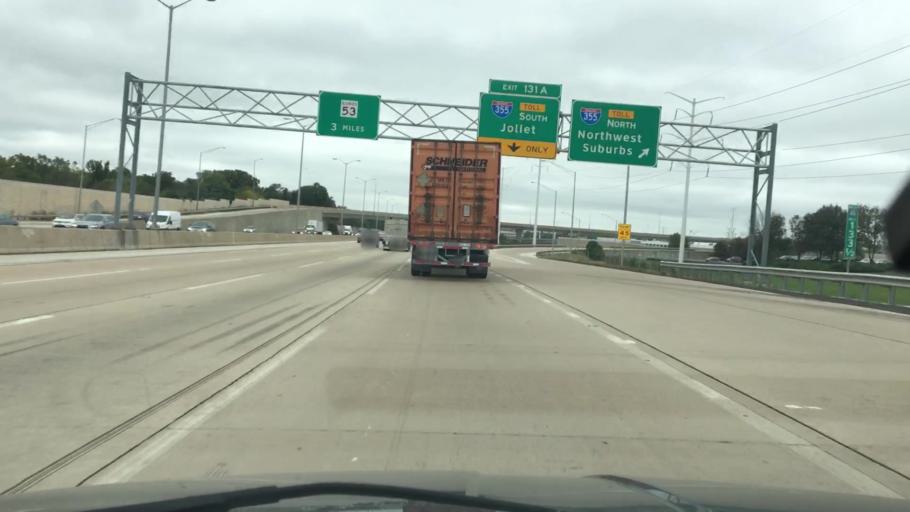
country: US
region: Illinois
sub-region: DuPage County
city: Downers Grove
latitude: 41.8267
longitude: -88.0223
